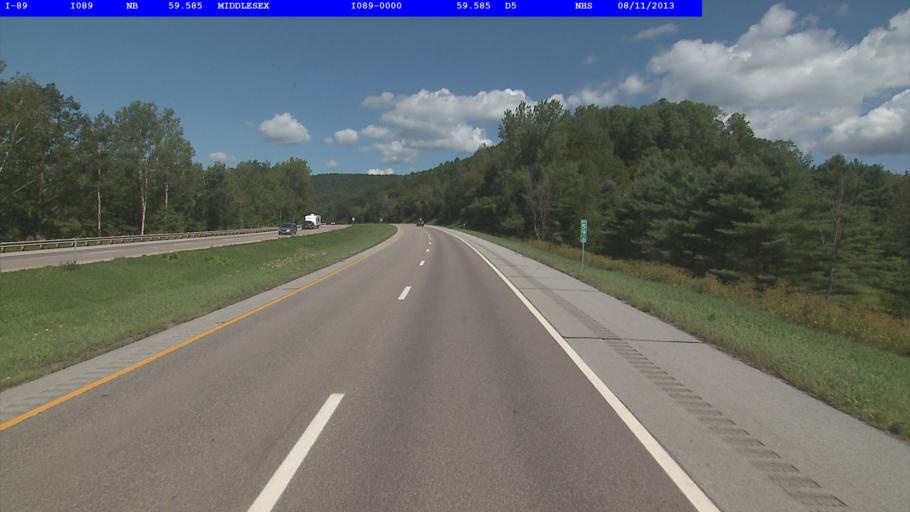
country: US
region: Vermont
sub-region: Washington County
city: Waterbury
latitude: 44.3093
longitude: -72.6927
